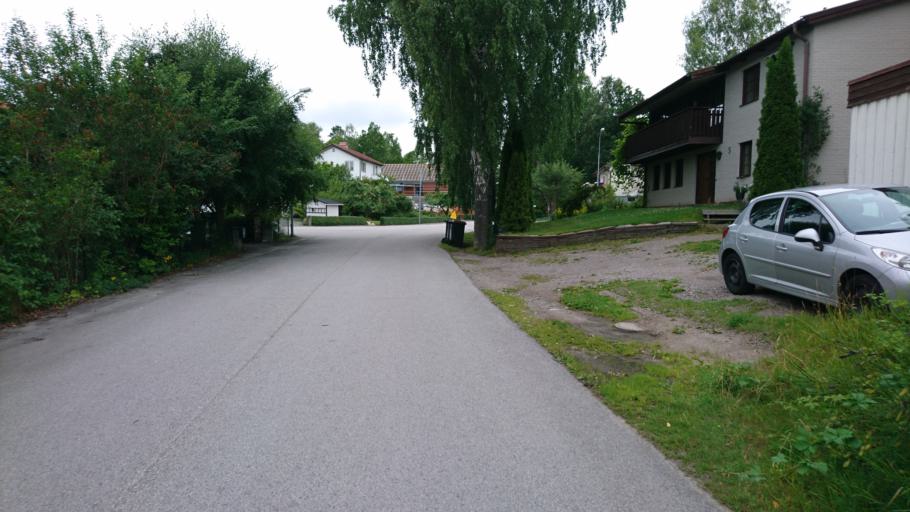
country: SE
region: Kalmar
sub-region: Vasterviks Kommun
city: Vaestervik
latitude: 57.7225
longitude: 16.5284
